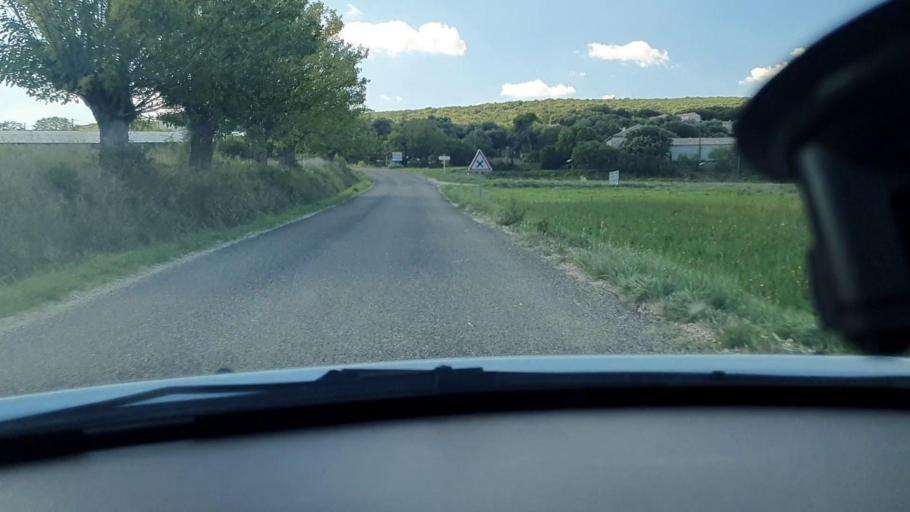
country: FR
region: Languedoc-Roussillon
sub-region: Departement du Gard
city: Goudargues
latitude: 44.1730
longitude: 4.4474
